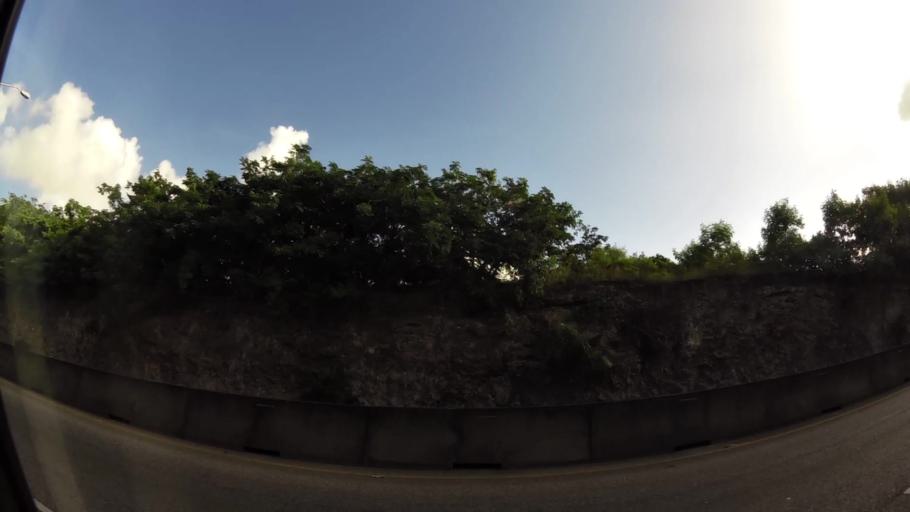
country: BB
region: Saint Michael
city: Bridgetown
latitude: 13.1391
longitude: -59.6008
